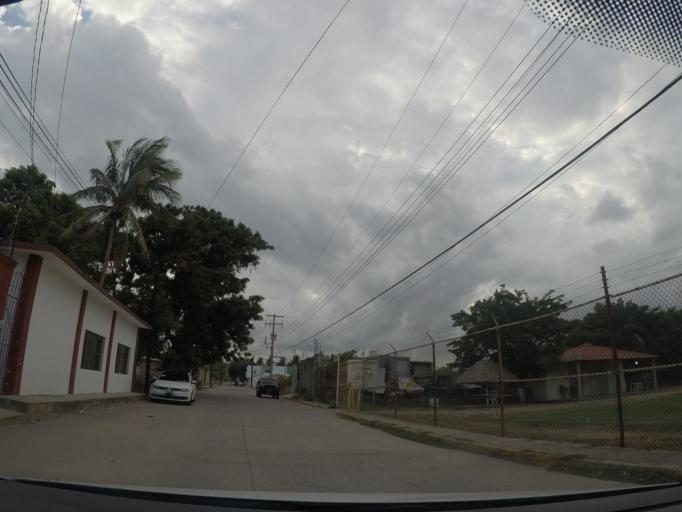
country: MX
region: Oaxaca
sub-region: Salina Cruz
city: Salina Cruz
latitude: 16.2139
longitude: -95.1949
